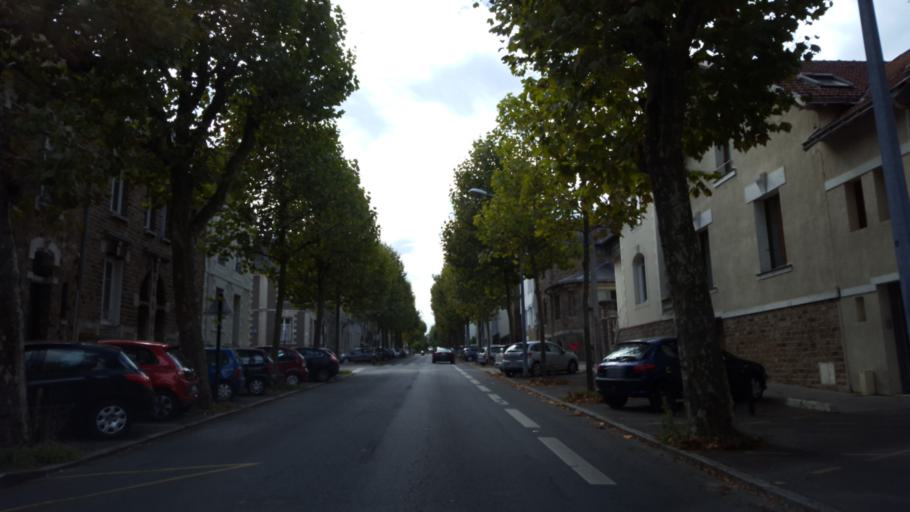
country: FR
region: Pays de la Loire
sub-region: Departement de la Loire-Atlantique
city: Nantes
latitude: 47.2056
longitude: -1.5800
